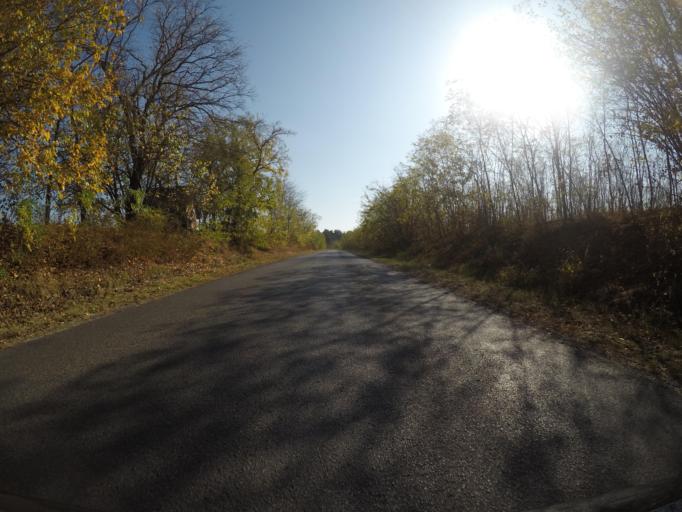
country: HU
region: Tolna
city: Nagydorog
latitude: 46.6347
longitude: 18.6782
